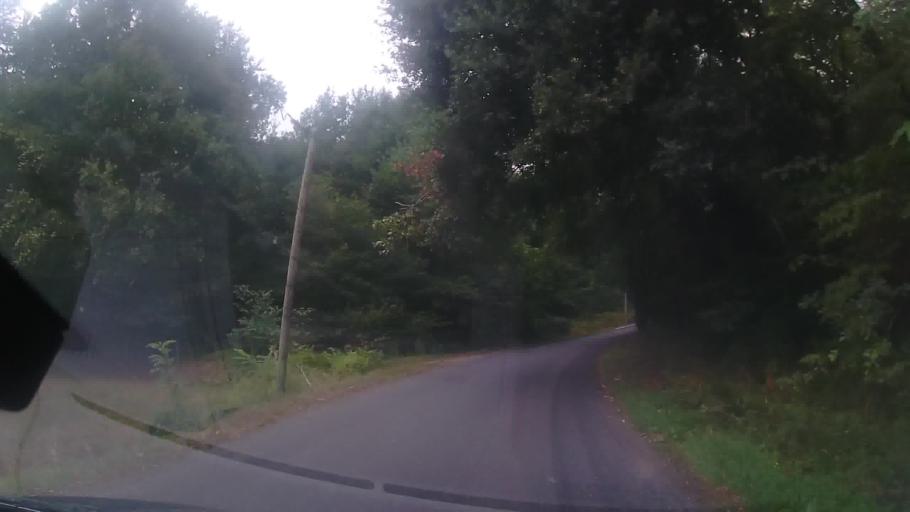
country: FR
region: Aquitaine
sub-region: Departement de la Dordogne
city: Eyvigues-et-Eybenes
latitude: 44.8396
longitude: 1.3609
